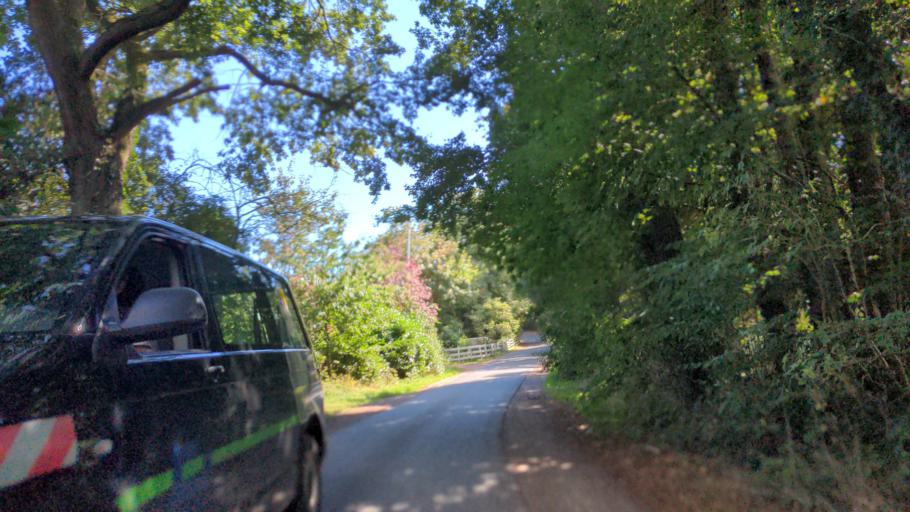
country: DE
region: Schleswig-Holstein
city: Kasseedorf
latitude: 54.1421
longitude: 10.7233
